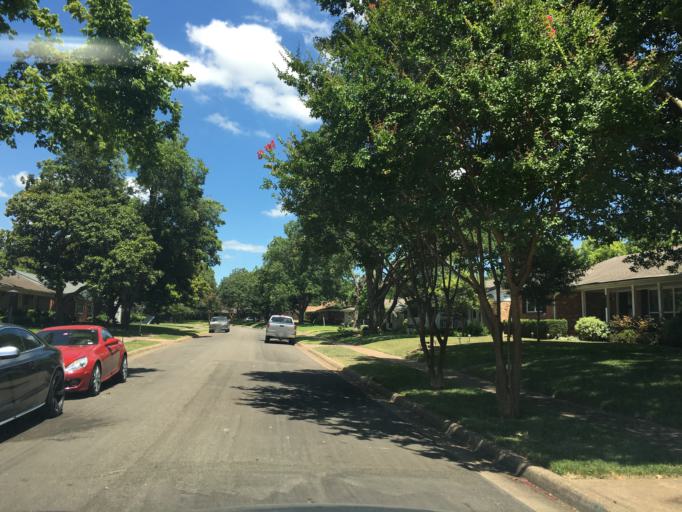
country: US
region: Texas
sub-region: Dallas County
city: Garland
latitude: 32.8495
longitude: -96.6933
